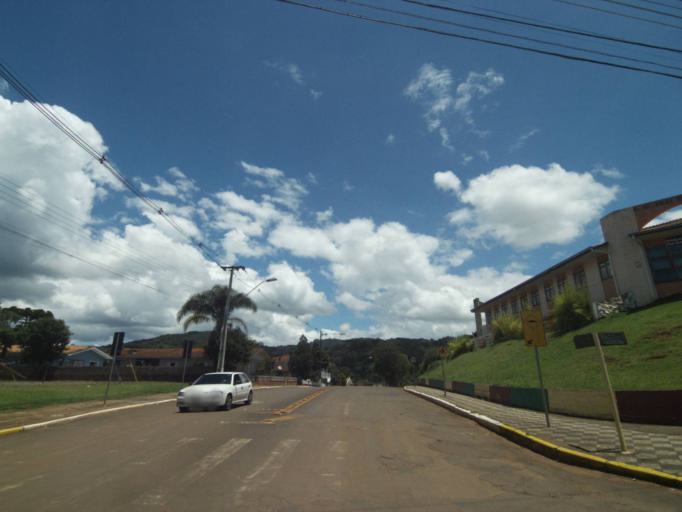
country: BR
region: Parana
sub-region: Uniao Da Vitoria
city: Uniao da Vitoria
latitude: -26.1642
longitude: -51.5550
